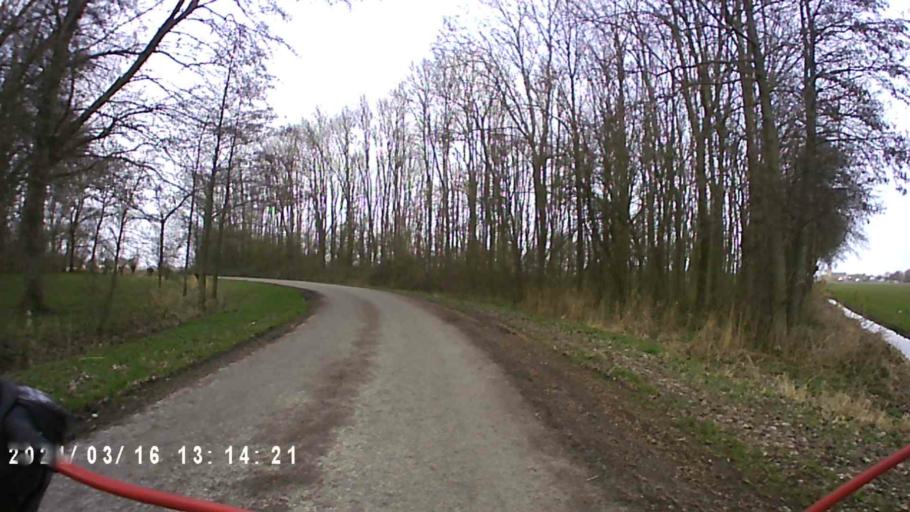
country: NL
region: Friesland
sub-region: Gemeente Het Bildt
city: Minnertsga
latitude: 53.2397
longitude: 5.6036
